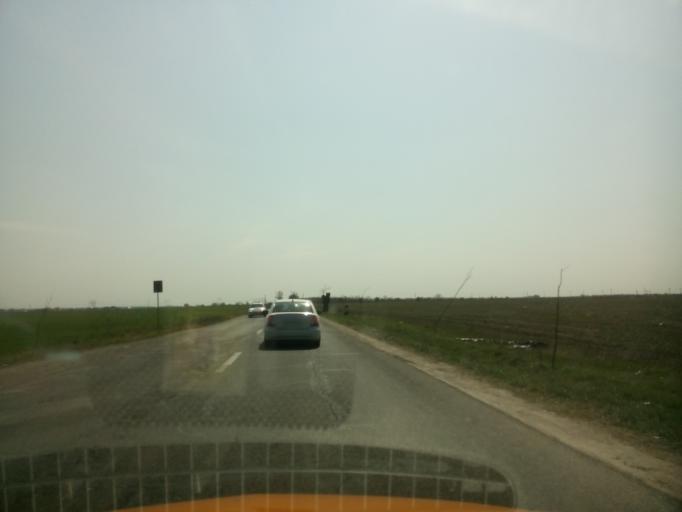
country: RO
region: Ilfov
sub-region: Comuna Glina
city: Glina
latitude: 44.3349
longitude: 26.2442
